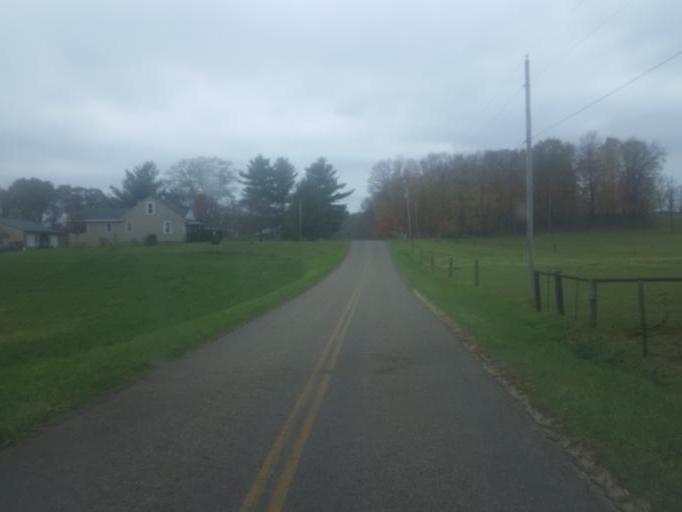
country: US
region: Ohio
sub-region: Richland County
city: Lincoln Heights
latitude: 40.7417
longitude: -82.4220
